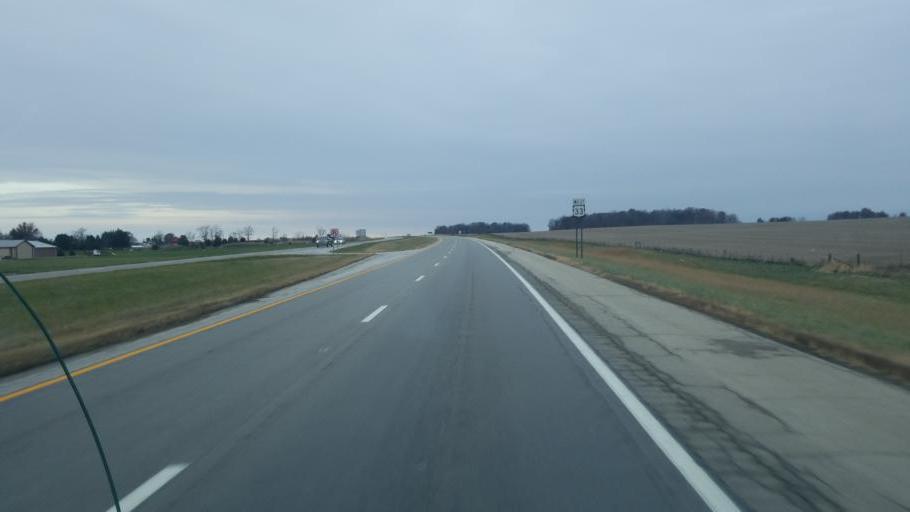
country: US
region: Ohio
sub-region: Auglaize County
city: Wapakoneta
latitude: 40.5659
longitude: -84.2401
